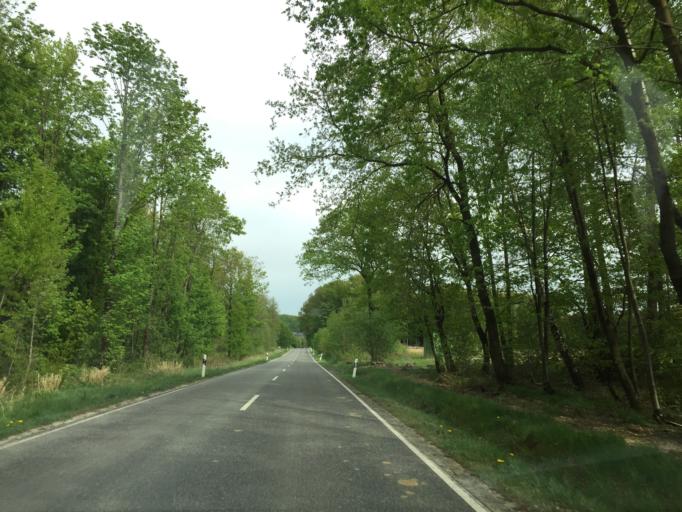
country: DE
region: Rheinland-Pfalz
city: Berod bei Wallmerod
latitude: 50.4840
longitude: 7.9174
